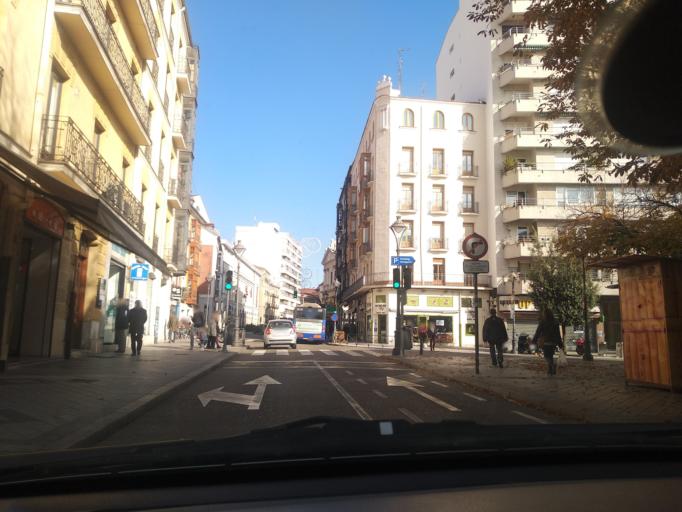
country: ES
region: Castille and Leon
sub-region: Provincia de Valladolid
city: Valladolid
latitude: 41.6530
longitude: -4.7248
